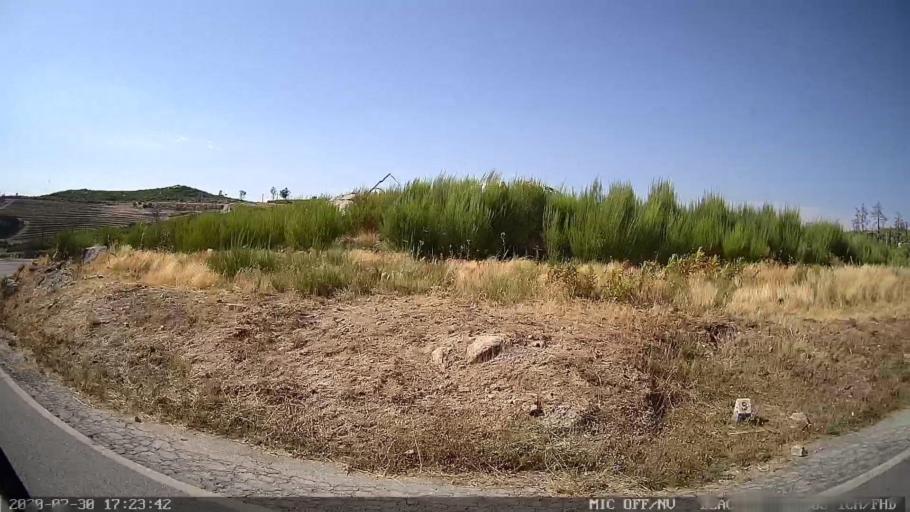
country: PT
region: Vila Real
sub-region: Murca
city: Murca
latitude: 41.3090
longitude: -7.4683
